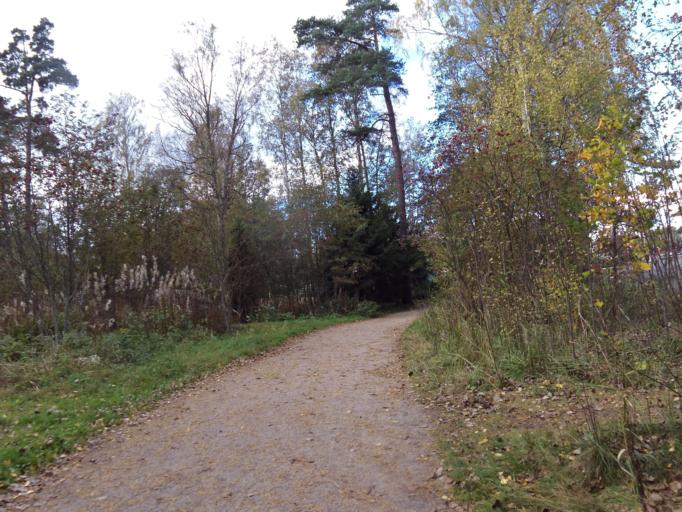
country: FI
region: Uusimaa
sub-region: Helsinki
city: Koukkuniemi
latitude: 60.1543
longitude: 24.7746
